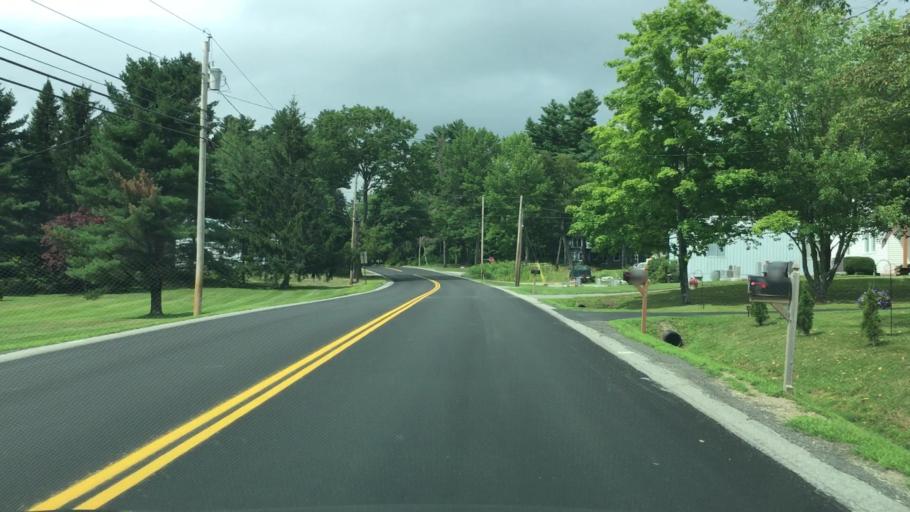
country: US
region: Maine
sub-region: Hancock County
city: Bucksport
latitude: 44.6030
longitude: -68.8166
